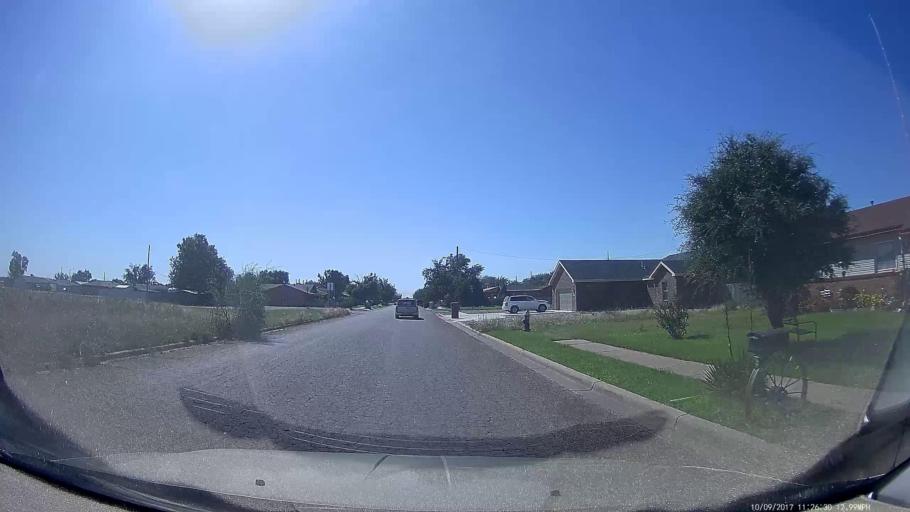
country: US
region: New Mexico
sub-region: Curry County
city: Clovis
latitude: 34.4104
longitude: -103.2273
